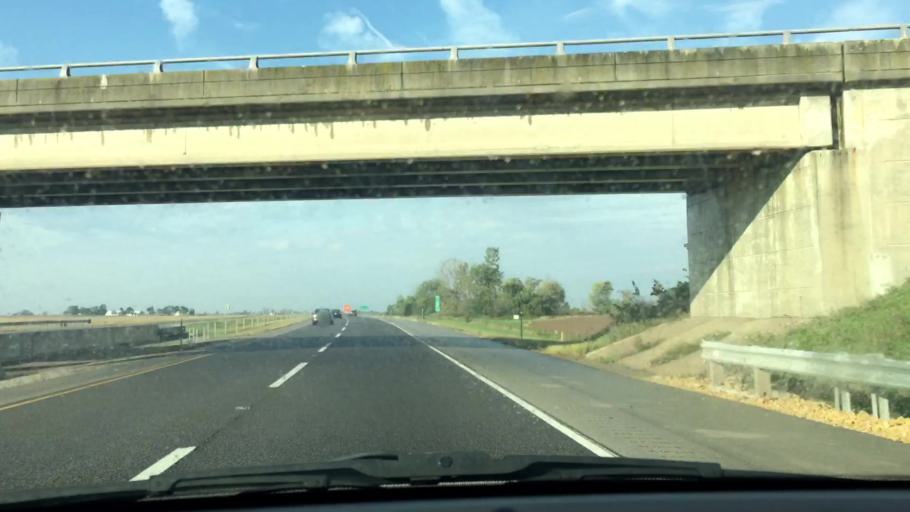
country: US
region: Illinois
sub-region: Lee County
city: Franklin Grove
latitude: 41.8528
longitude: -89.2265
